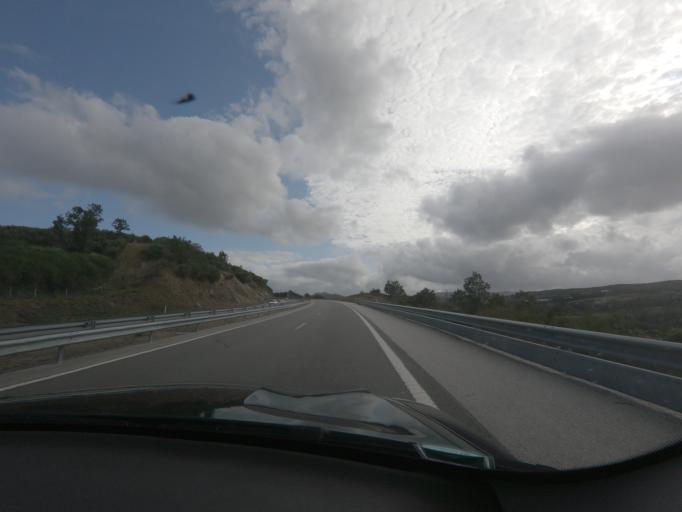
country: PT
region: Viseu
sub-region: Tarouca
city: Tarouca
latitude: 41.0178
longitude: -7.8814
